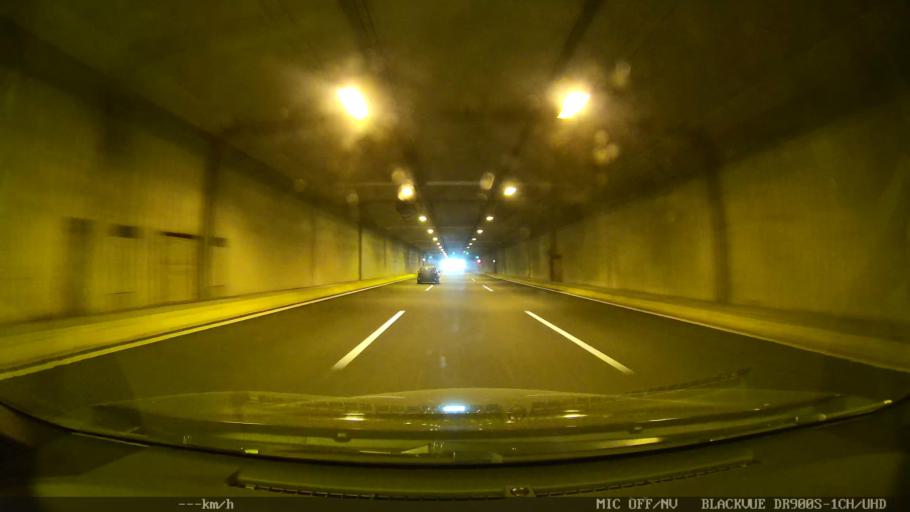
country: GR
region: Central Macedonia
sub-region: Nomos Pierias
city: Katerini
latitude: 40.2732
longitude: 22.5223
